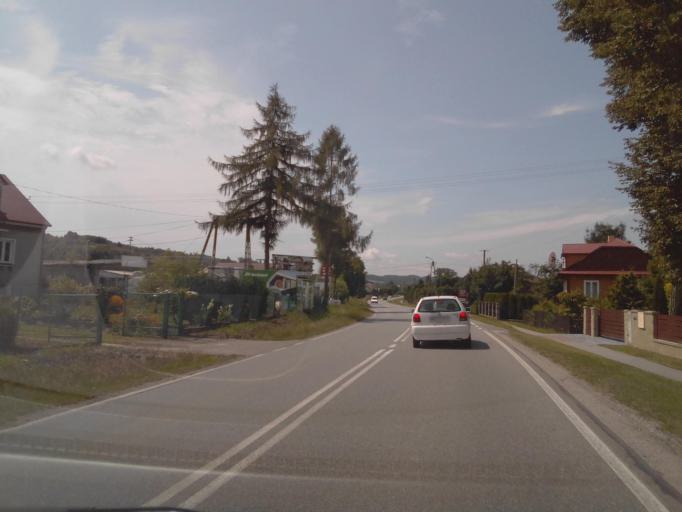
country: PL
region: Subcarpathian Voivodeship
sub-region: Powiat ropczycko-sedziszowski
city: Ropczyce
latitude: 50.0465
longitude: 21.5950
